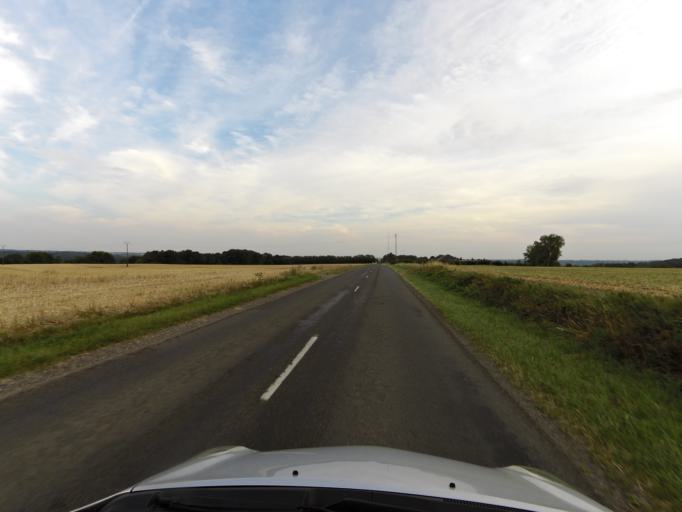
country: FR
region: Picardie
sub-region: Departement de l'Aisne
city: Bruyeres-et-Montberault
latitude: 49.4950
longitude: 3.6699
